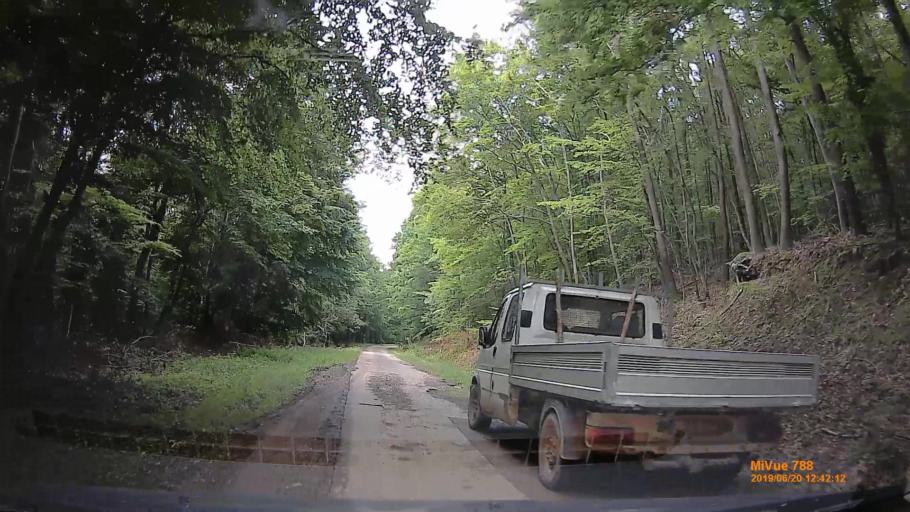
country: HU
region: Baranya
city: Hosszuheteny
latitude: 46.1980
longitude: 18.3618
